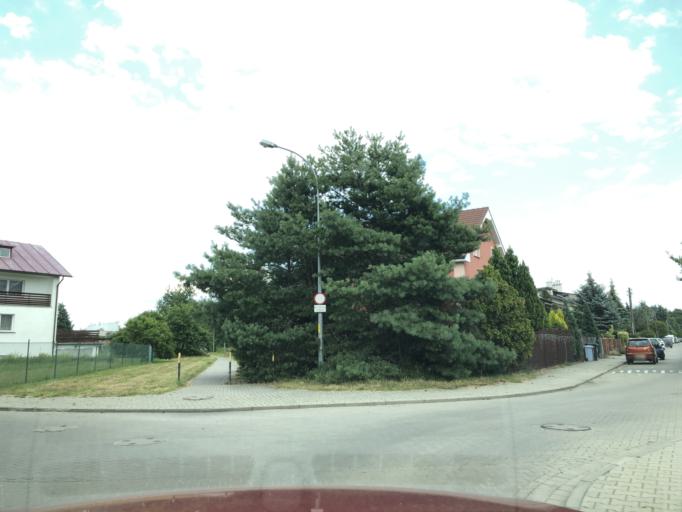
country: PL
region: Lower Silesian Voivodeship
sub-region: Powiat wroclawski
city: Smolec
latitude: 51.1534
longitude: 16.9088
